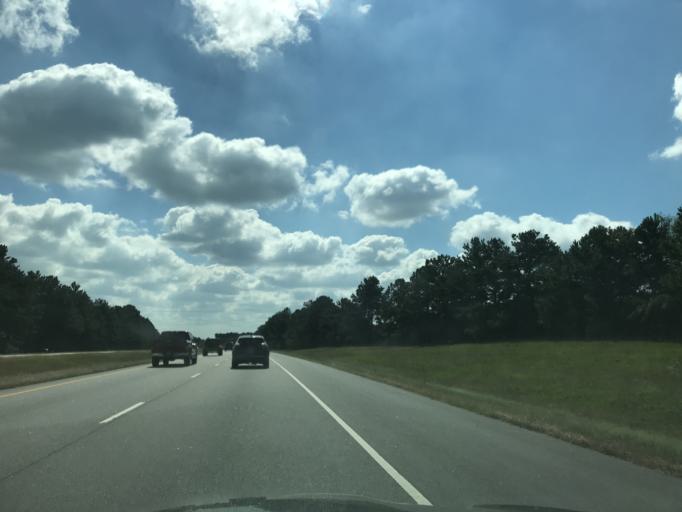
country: US
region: North Carolina
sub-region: Wake County
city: Wake Forest
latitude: 35.9344
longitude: -78.5430
